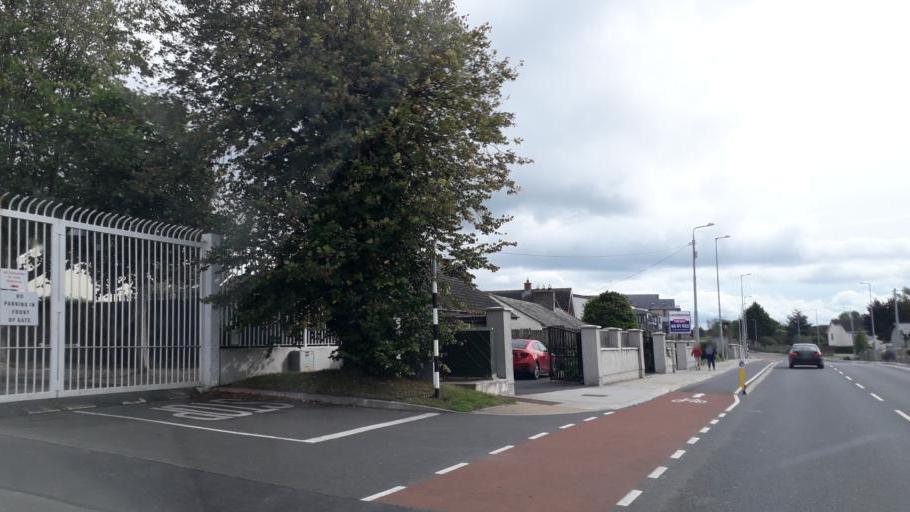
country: IE
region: Leinster
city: Cabinteely
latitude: 53.2698
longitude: -6.1507
